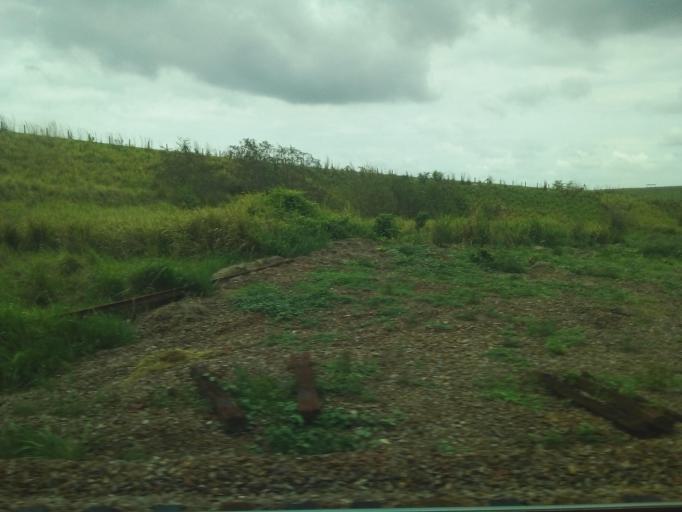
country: BR
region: Maranhao
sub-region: Santa Ines
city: Santa Ines
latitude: -3.7235
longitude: -45.5088
